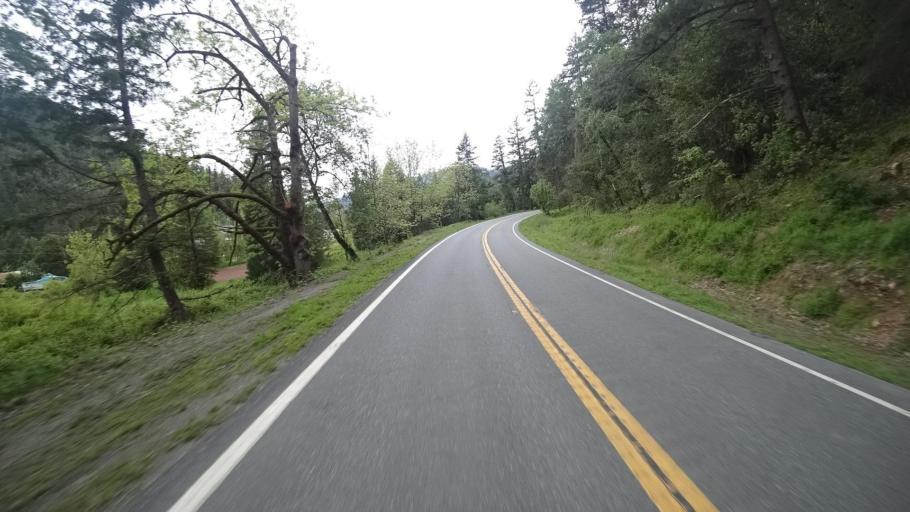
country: US
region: California
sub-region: Humboldt County
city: Willow Creek
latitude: 40.9875
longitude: -123.6370
